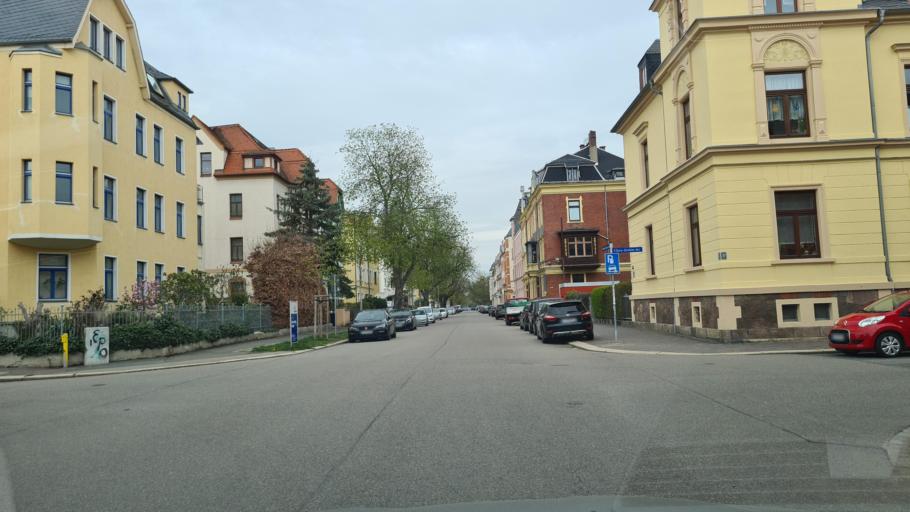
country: DE
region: Saxony
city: Zwickau
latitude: 50.7274
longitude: 12.4890
